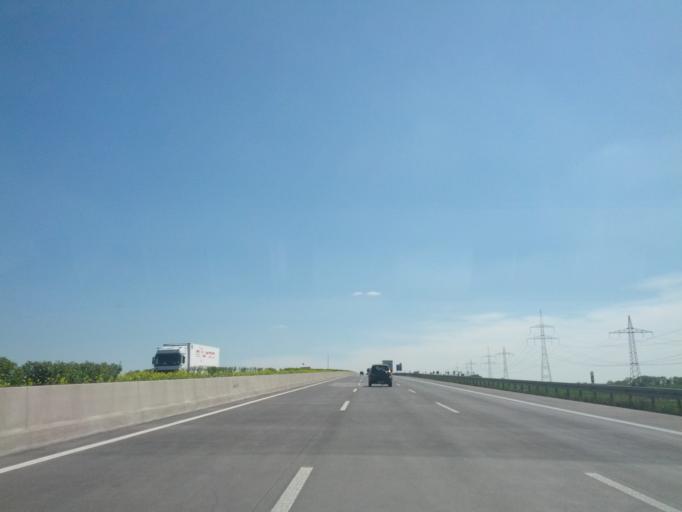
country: DE
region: Thuringia
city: Seebach
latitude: 50.9948
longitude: 10.4299
